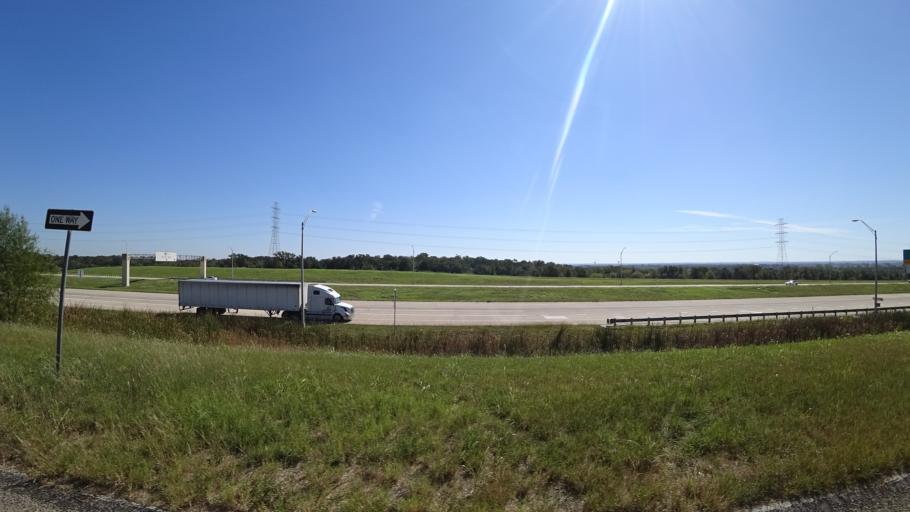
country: US
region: Texas
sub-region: Travis County
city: Hornsby Bend
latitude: 30.2643
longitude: -97.5985
